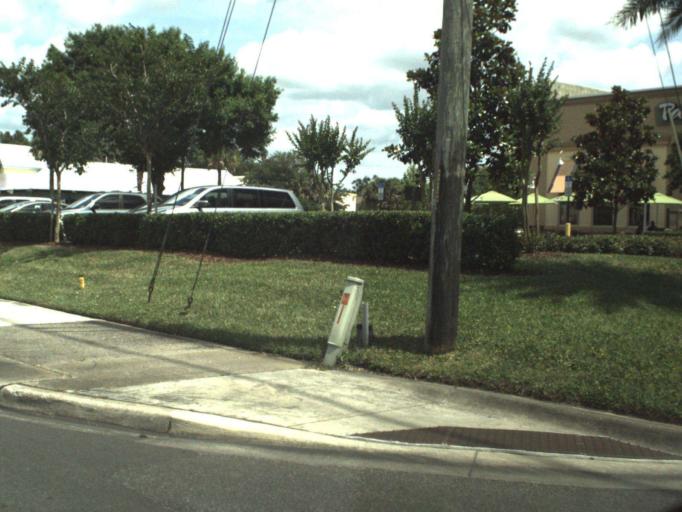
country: US
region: Florida
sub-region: Orange County
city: Winter Park
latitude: 28.6015
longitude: -81.3196
